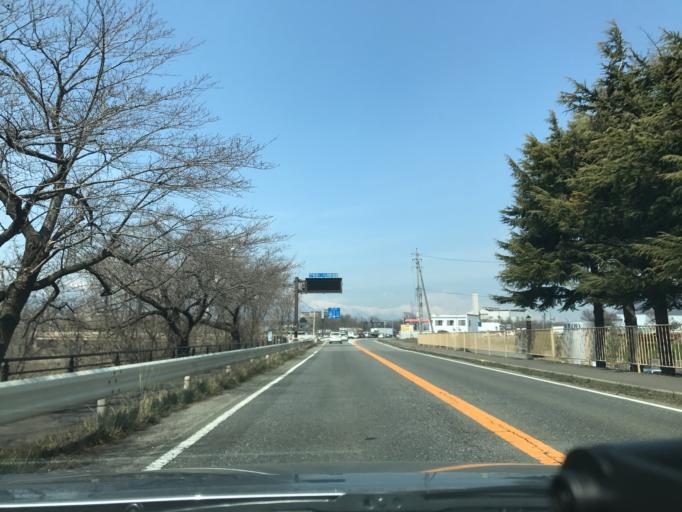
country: JP
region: Nagano
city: Matsumoto
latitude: 36.2642
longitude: 137.9457
